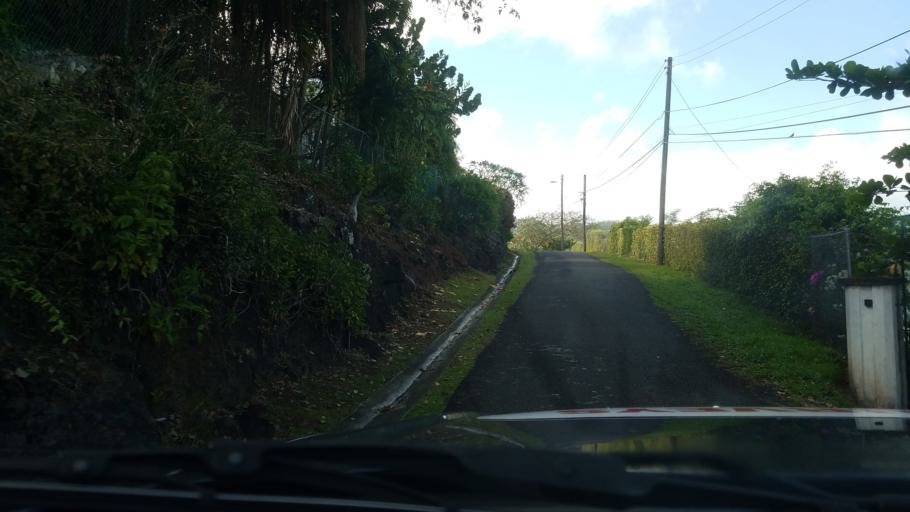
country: LC
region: Castries Quarter
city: Castries
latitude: 14.0207
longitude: -61.0020
